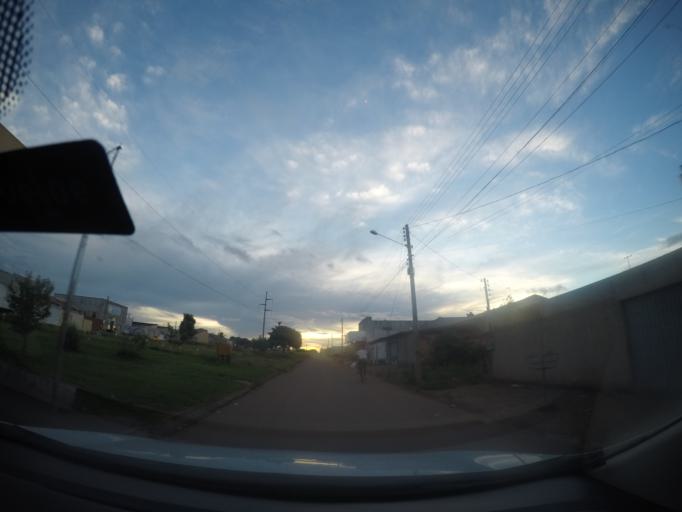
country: BR
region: Goias
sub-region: Goianira
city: Goianira
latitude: -16.5719
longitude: -49.3850
